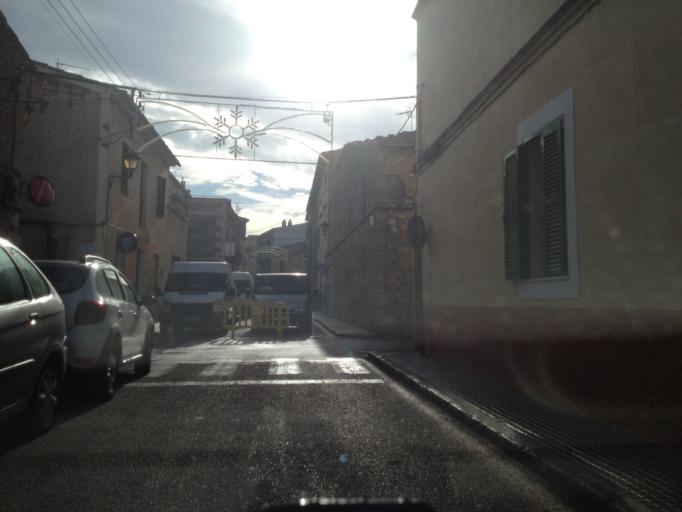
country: ES
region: Balearic Islands
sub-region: Illes Balears
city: Son Servera
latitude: 39.6230
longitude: 3.3581
